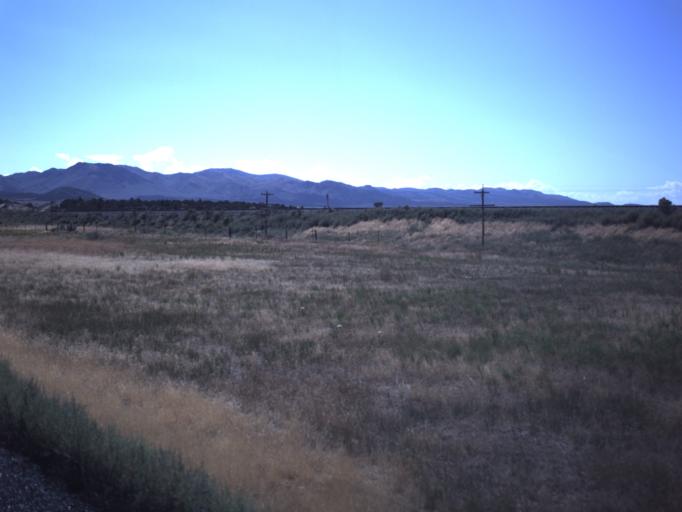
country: US
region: Utah
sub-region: Utah County
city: Genola
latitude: 39.9397
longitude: -112.1854
